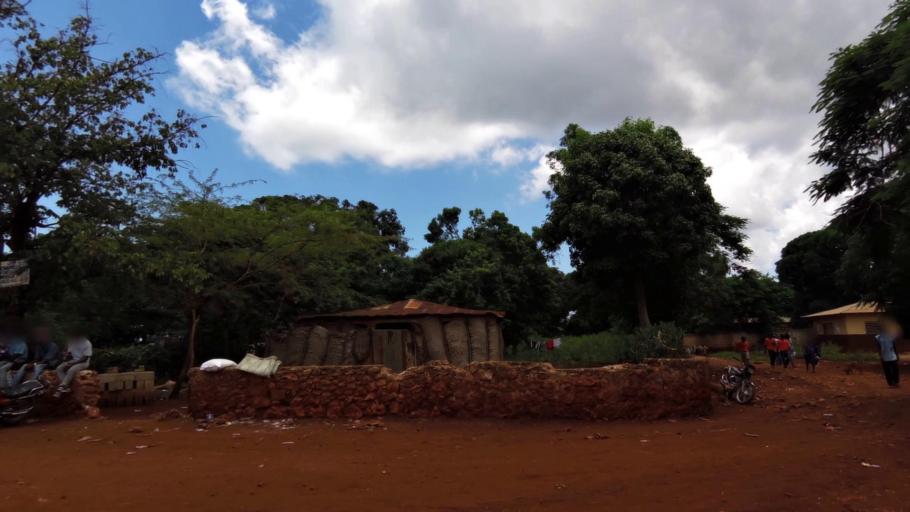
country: HT
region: Ouest
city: Anse a Galets
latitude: 18.7793
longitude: -72.8604
